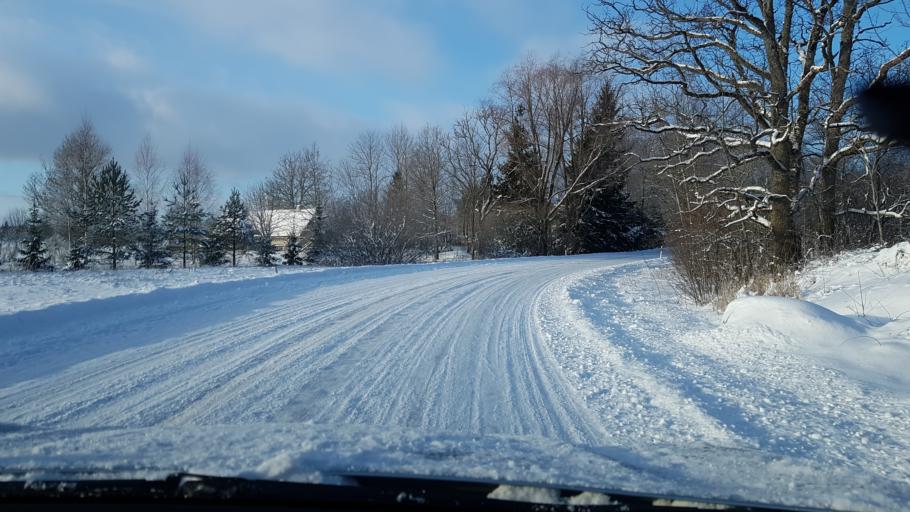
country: EE
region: Harju
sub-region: Nissi vald
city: Turba
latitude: 59.1051
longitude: 24.2365
